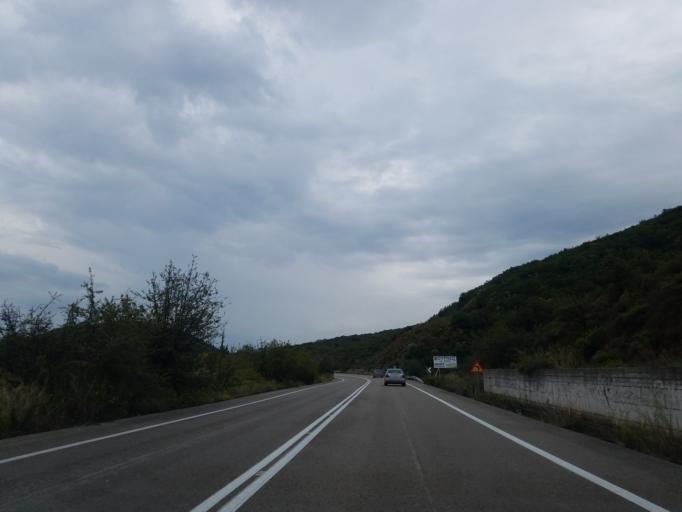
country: GR
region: Central Greece
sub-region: Nomos Voiotias
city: Livadeia
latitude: 38.4452
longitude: 22.7998
